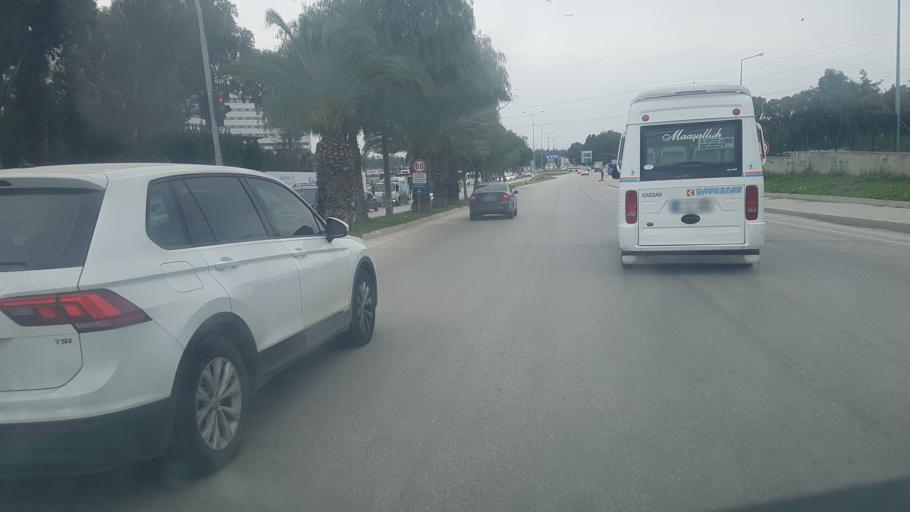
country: TR
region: Adana
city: Adana
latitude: 37.0321
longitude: 35.3462
